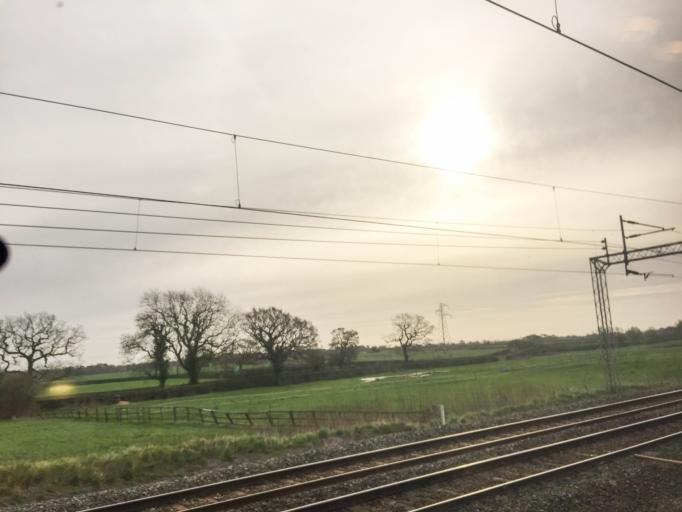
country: GB
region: England
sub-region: Cheshire West and Chester
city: Winsford
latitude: 53.1795
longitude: -2.4851
